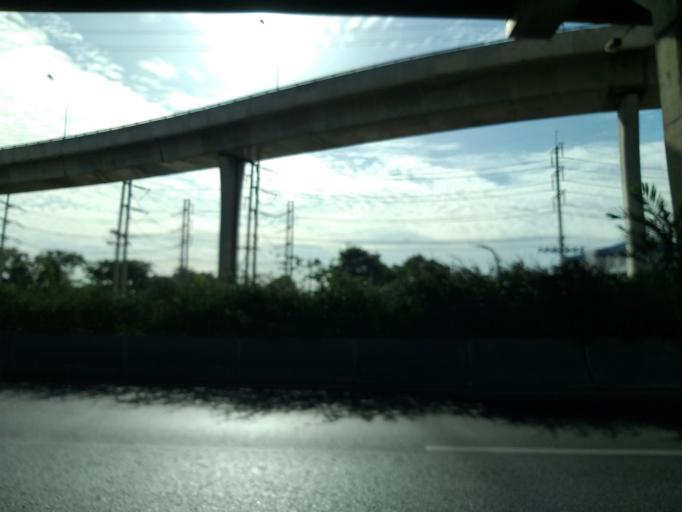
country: TH
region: Bangkok
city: Sai Mai
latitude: 13.9788
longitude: 100.6171
